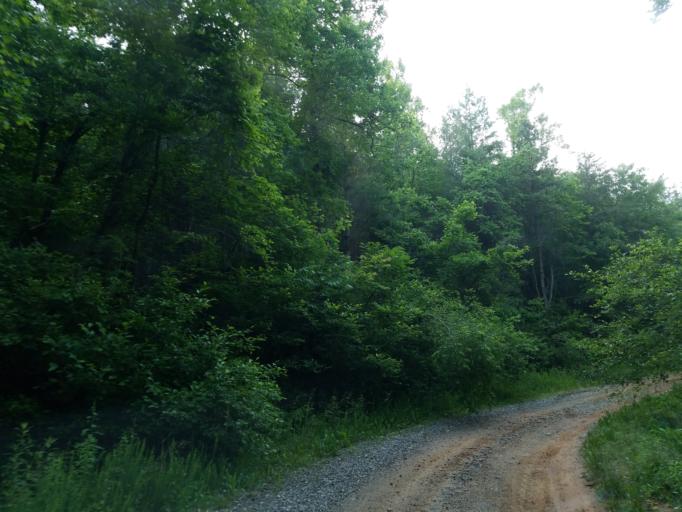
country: US
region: Georgia
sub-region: Dawson County
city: Dawsonville
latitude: 34.5691
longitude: -84.1372
